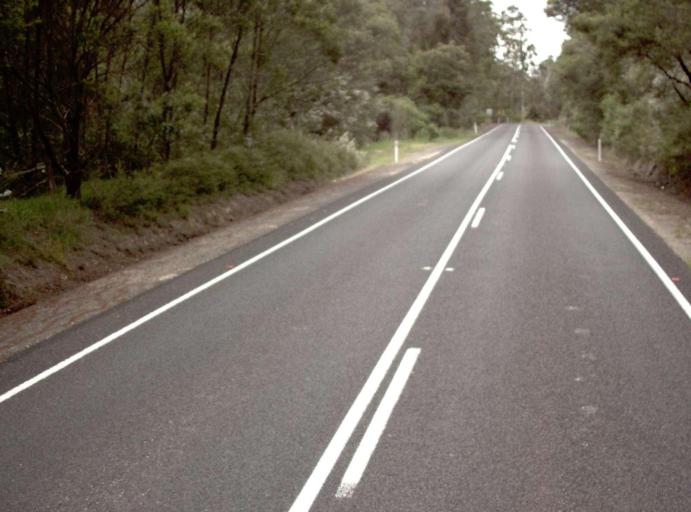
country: AU
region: New South Wales
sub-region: Bombala
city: Bombala
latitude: -37.4142
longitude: 149.1982
